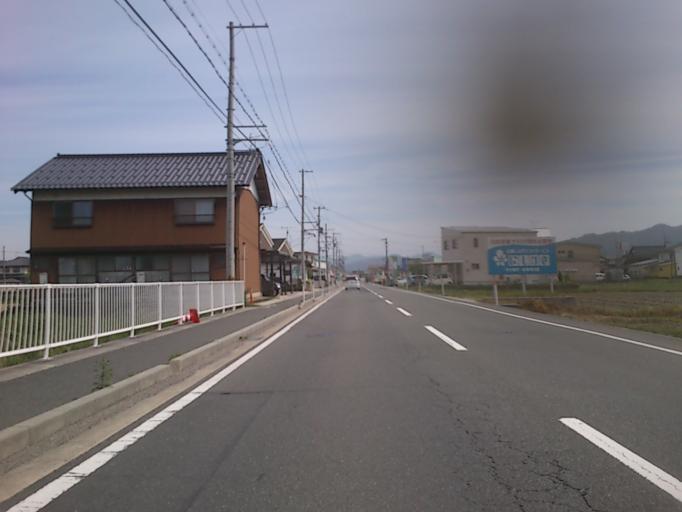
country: JP
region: Kyoto
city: Miyazu
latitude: 35.6239
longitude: 135.0734
